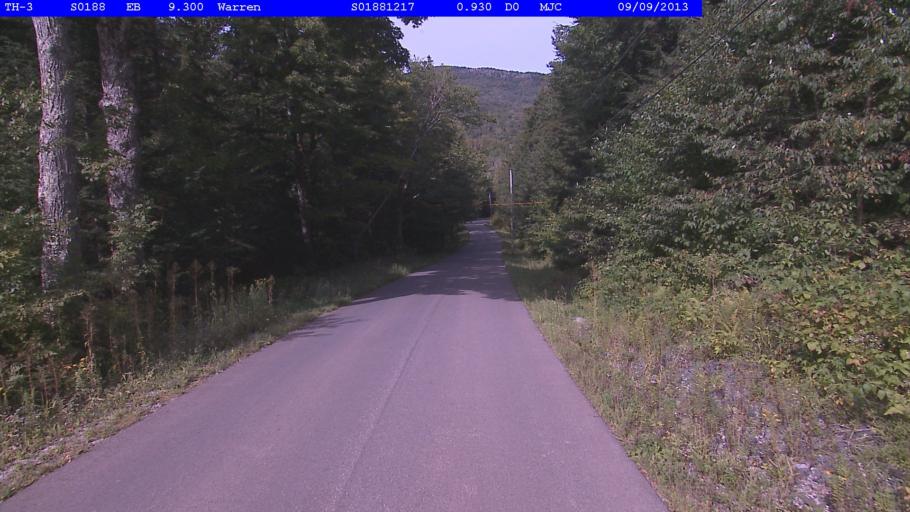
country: US
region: Vermont
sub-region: Addison County
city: Bristol
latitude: 44.0952
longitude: -72.9102
